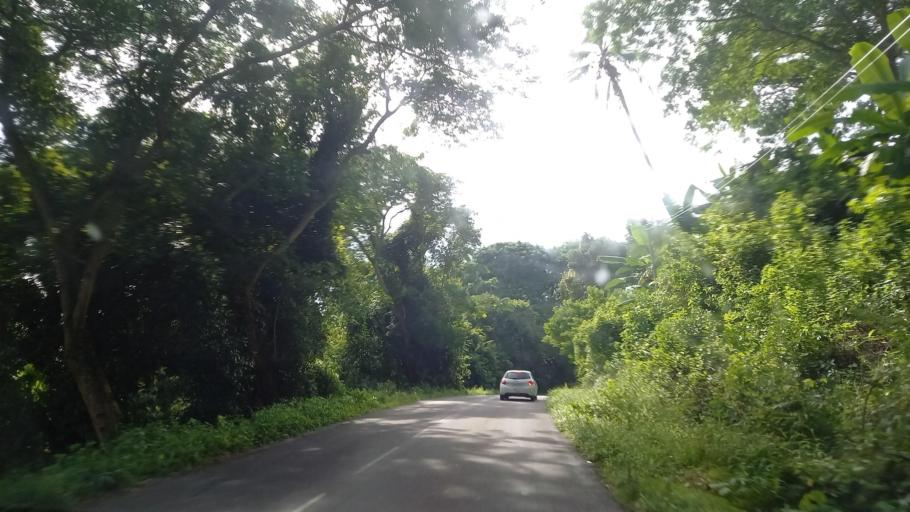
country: YT
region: Ouangani
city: Ouangani
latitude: -12.8862
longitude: 45.1325
